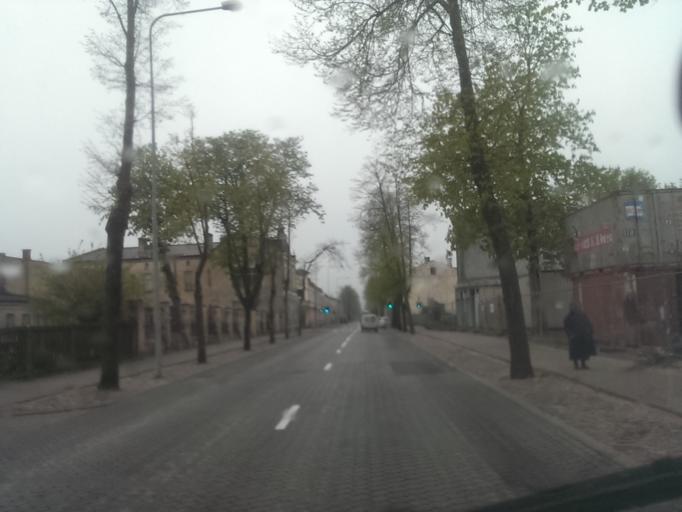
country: LV
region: Ventspils
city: Ventspils
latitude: 57.3918
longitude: 21.5616
